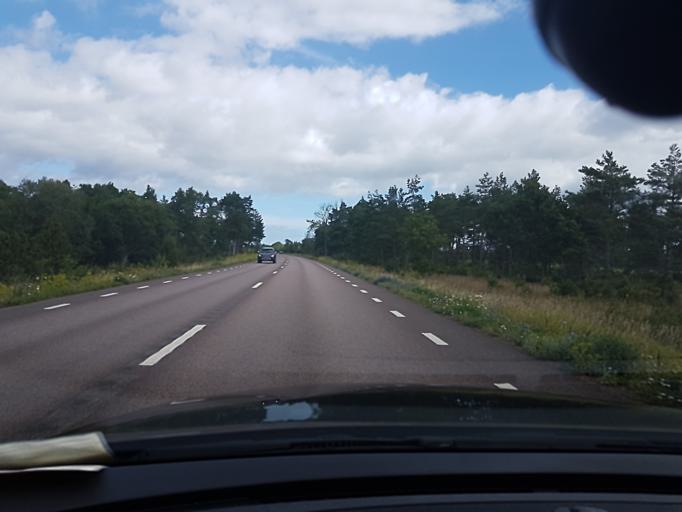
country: SE
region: Kalmar
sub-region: Borgholms Kommun
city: Borgholm
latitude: 57.0821
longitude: 16.9197
